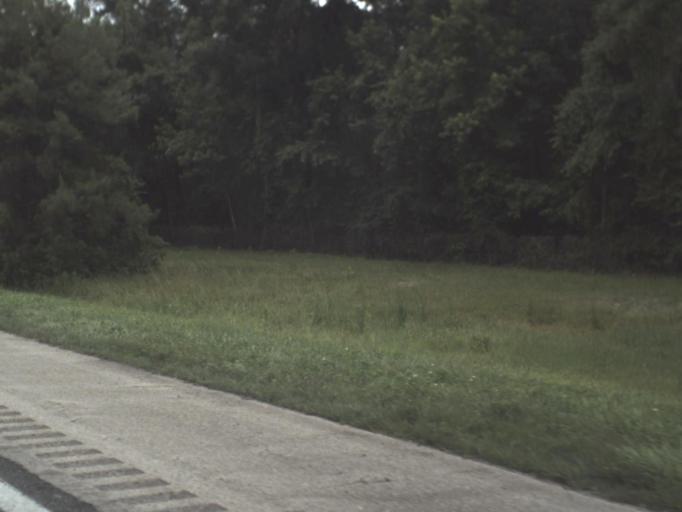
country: US
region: Florida
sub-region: Alachua County
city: Gainesville
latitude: 29.5333
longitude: -82.3204
